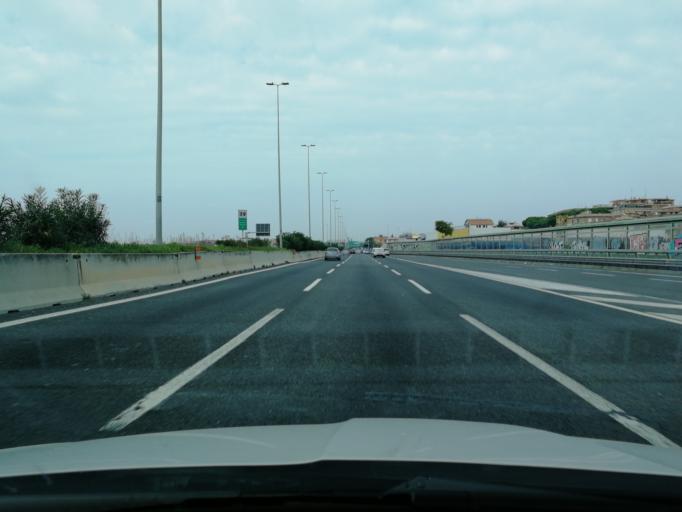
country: IT
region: Latium
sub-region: Citta metropolitana di Roma Capitale
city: Ciampino
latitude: 41.8561
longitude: 12.5984
